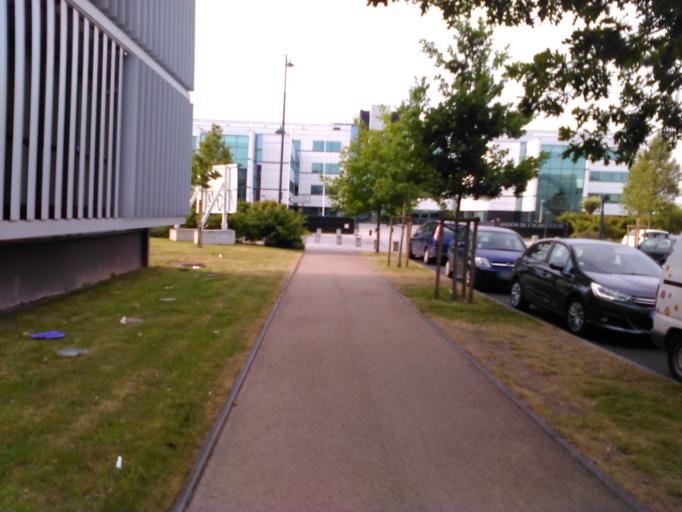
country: FR
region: Brittany
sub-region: Departement d'Ille-et-Vilaine
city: Rennes
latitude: 48.1152
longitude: -1.7137
